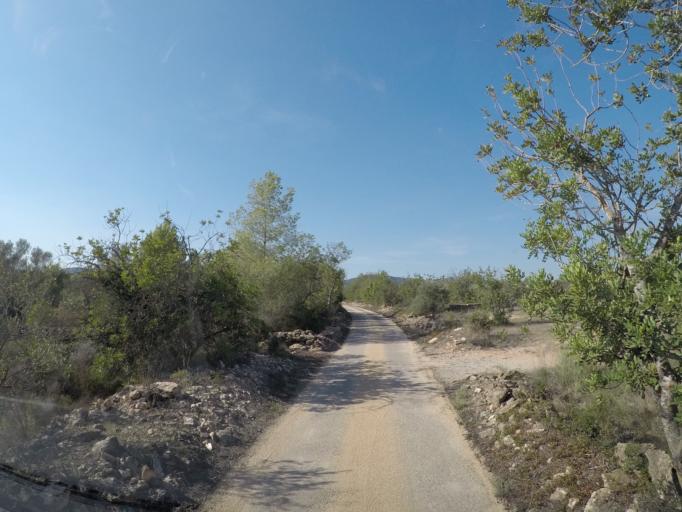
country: ES
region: Catalonia
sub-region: Provincia de Tarragona
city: El Perello
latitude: 40.9005
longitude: 0.7309
